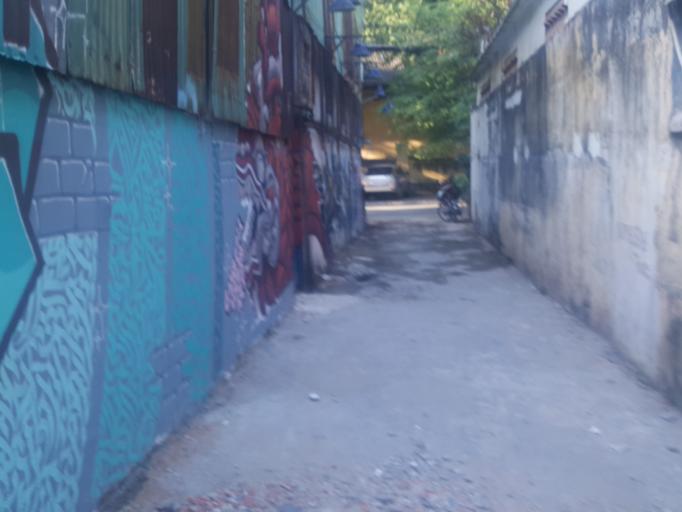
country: KH
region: Phnom Penh
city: Phnom Penh
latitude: 11.5605
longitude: 104.9303
